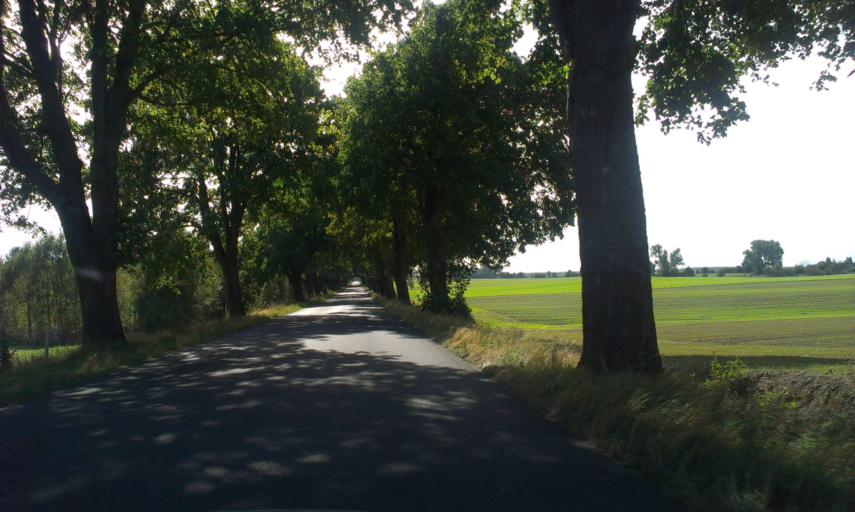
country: PL
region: Greater Poland Voivodeship
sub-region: Powiat zlotowski
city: Zlotow
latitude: 53.4660
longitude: 16.9882
